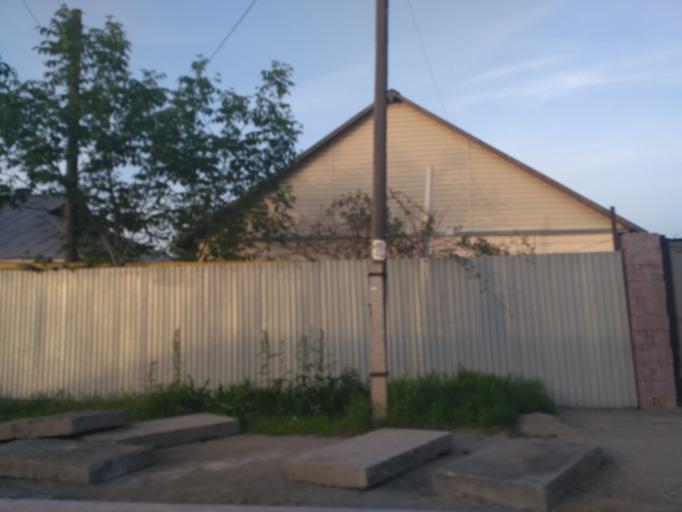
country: KZ
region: Almaty Qalasy
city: Almaty
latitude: 43.2190
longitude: 76.8313
